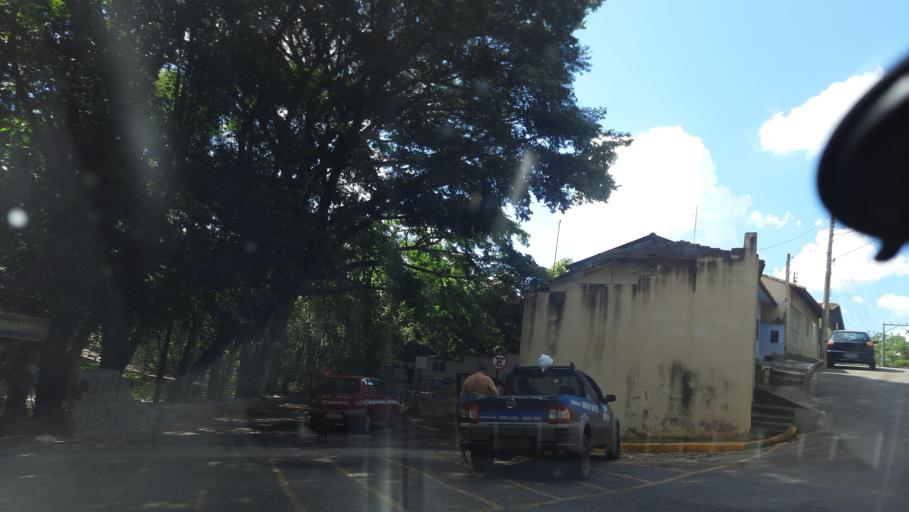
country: BR
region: Sao Paulo
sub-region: Sao Jose Do Rio Pardo
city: Sao Jose do Rio Pardo
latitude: -21.5919
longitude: -46.8948
